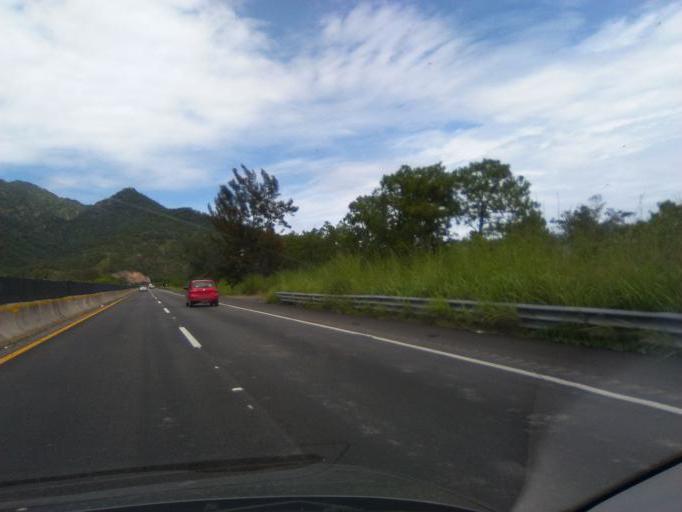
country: MX
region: Guerrero
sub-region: Chilpancingo de los Bravo
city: Cajelitos
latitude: 17.2897
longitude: -99.5049
